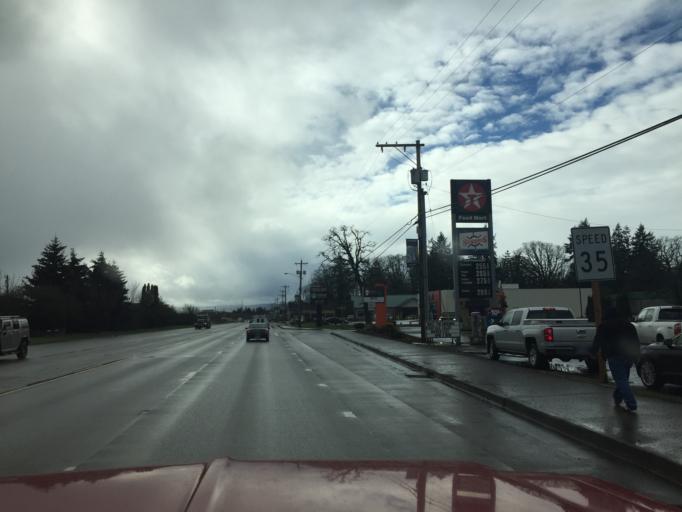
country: US
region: Oregon
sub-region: Columbia County
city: Saint Helens
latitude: 45.8559
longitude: -122.8245
